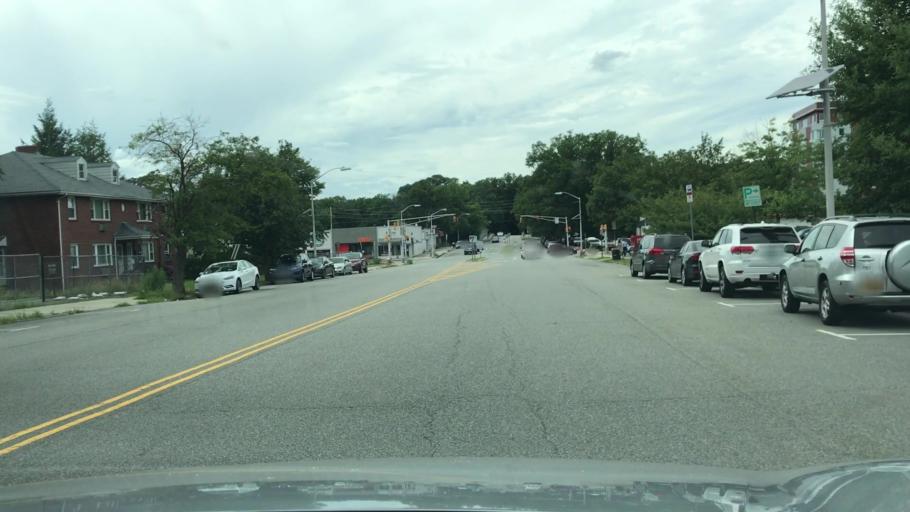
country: US
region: New Jersey
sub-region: Bergen County
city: Teaneck
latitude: 40.9024
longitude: -74.0028
